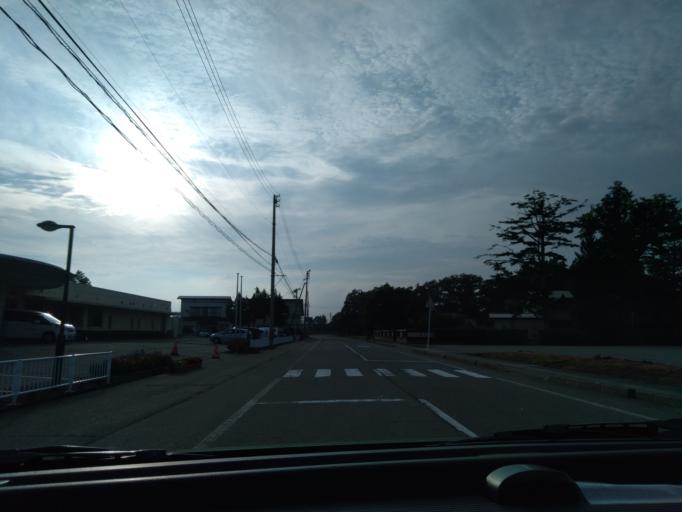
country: JP
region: Akita
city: Yokotemachi
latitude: 39.3869
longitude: 140.5286
